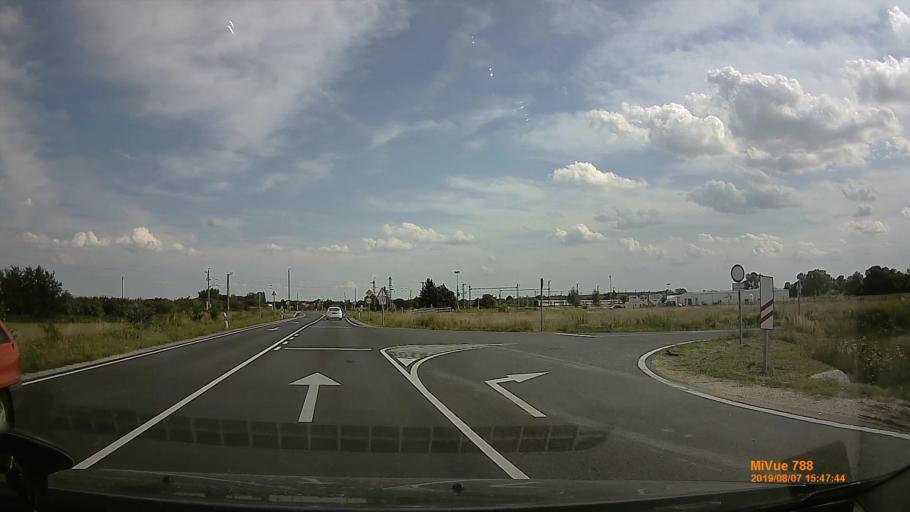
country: HU
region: Vas
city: Jak
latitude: 47.1674
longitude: 16.6304
